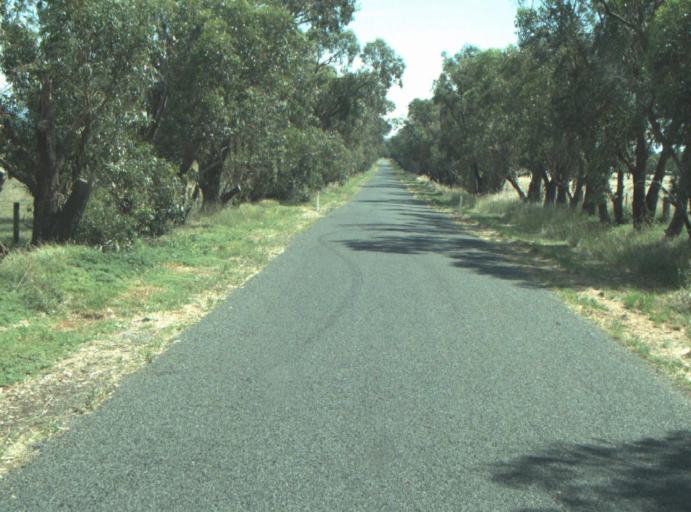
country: AU
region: Victoria
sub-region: Greater Geelong
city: Leopold
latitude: -38.1710
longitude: 144.4718
